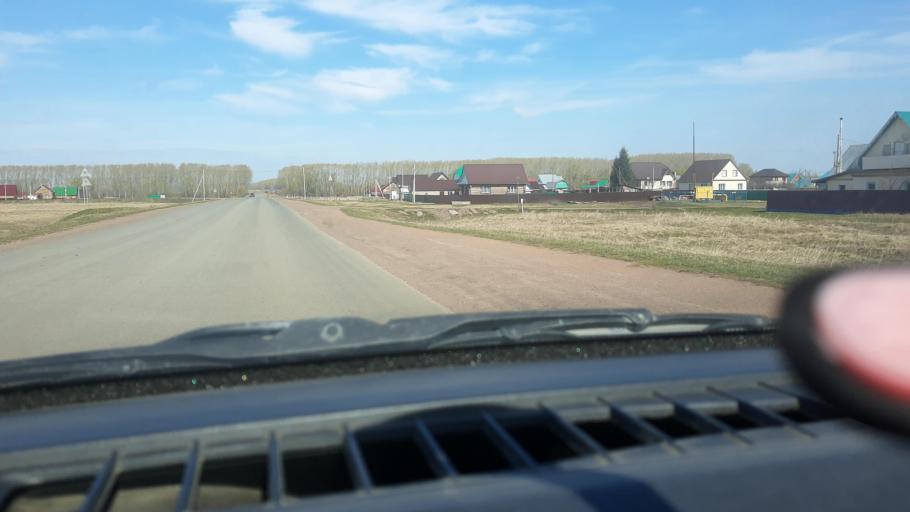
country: RU
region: Bashkortostan
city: Asanovo
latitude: 54.9656
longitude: 55.5443
